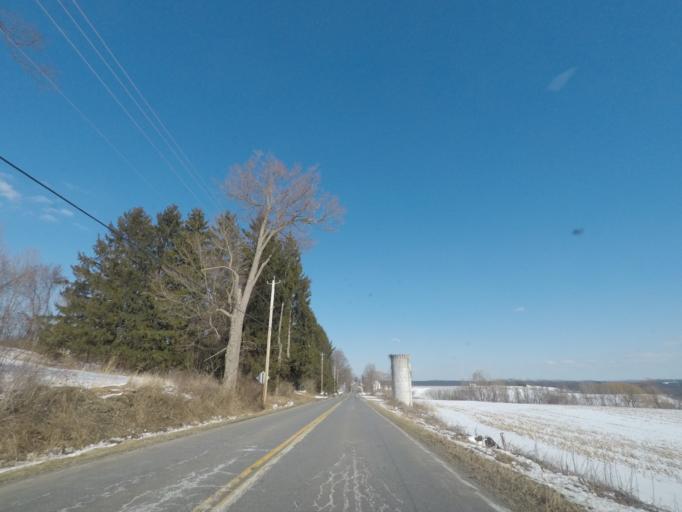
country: US
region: New York
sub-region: Saratoga County
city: Stillwater
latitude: 42.9147
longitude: -73.5491
